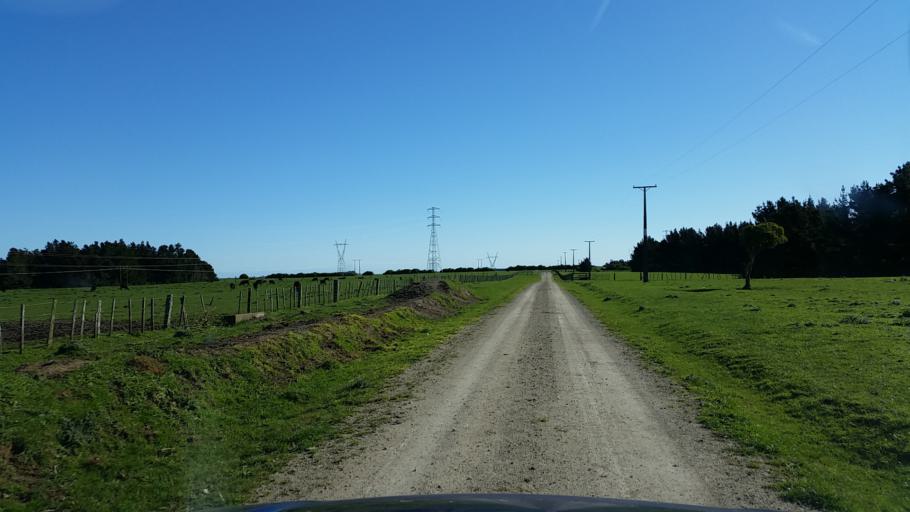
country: NZ
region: Taranaki
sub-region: South Taranaki District
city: Patea
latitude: -39.7891
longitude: 174.7543
